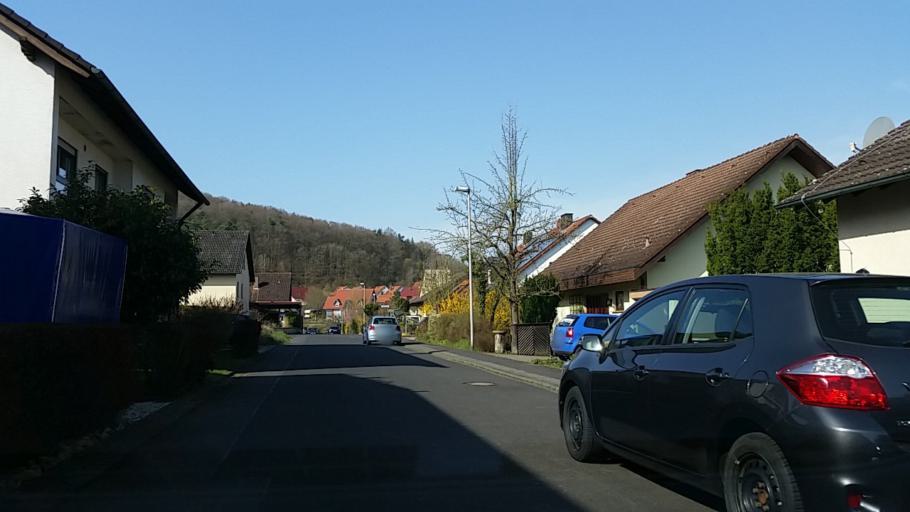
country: DE
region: Bavaria
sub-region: Regierungsbezirk Unterfranken
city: Himmelstadt
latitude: 49.9237
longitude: 9.7952
